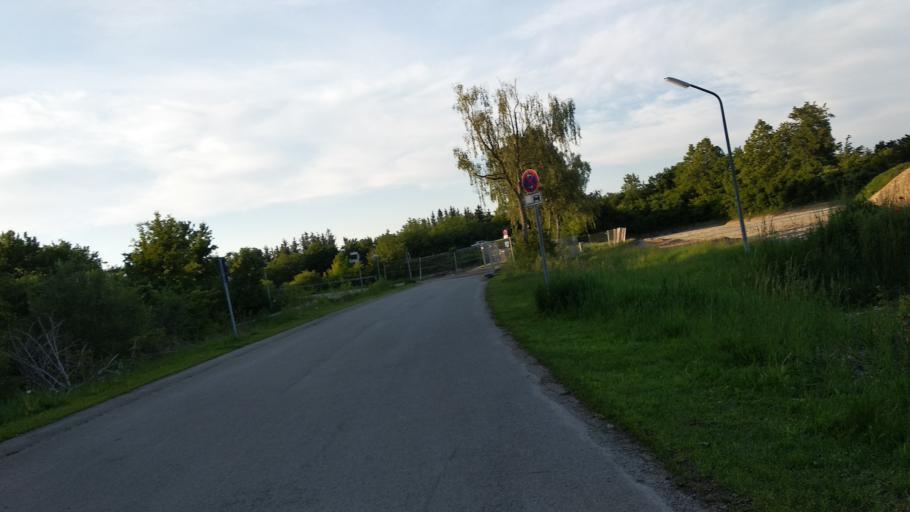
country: DE
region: Bavaria
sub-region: Upper Bavaria
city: Kirchheim bei Muenchen
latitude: 48.1703
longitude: 11.7540
